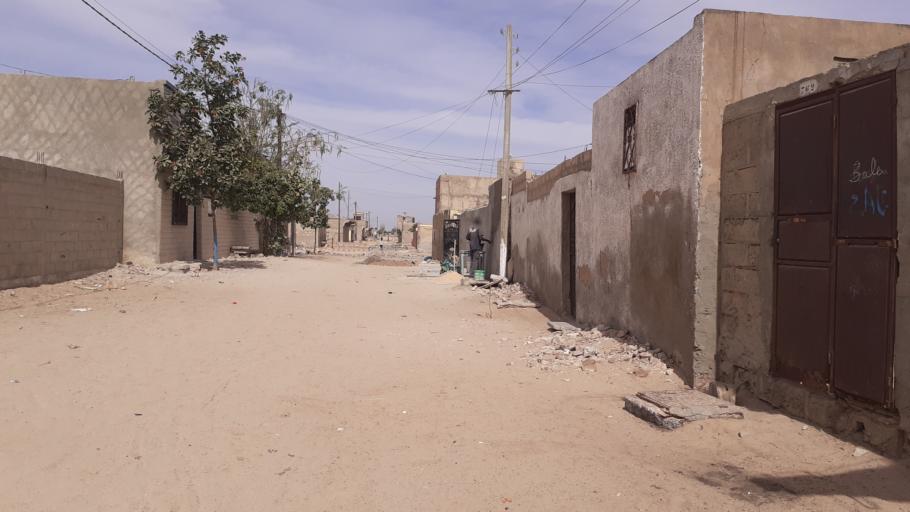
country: SN
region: Saint-Louis
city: Saint-Louis
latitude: 16.0238
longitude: -16.4840
